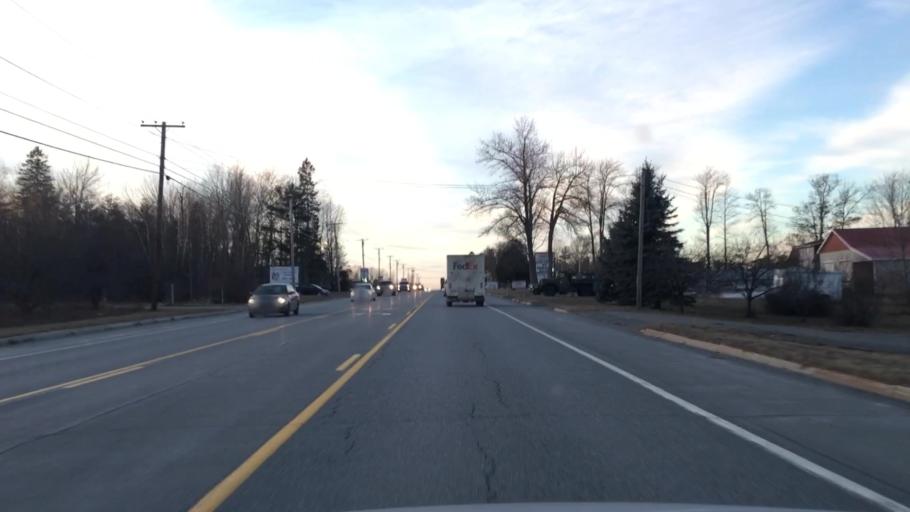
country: US
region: Maine
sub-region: Penobscot County
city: Holden
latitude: 44.7627
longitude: -68.7011
